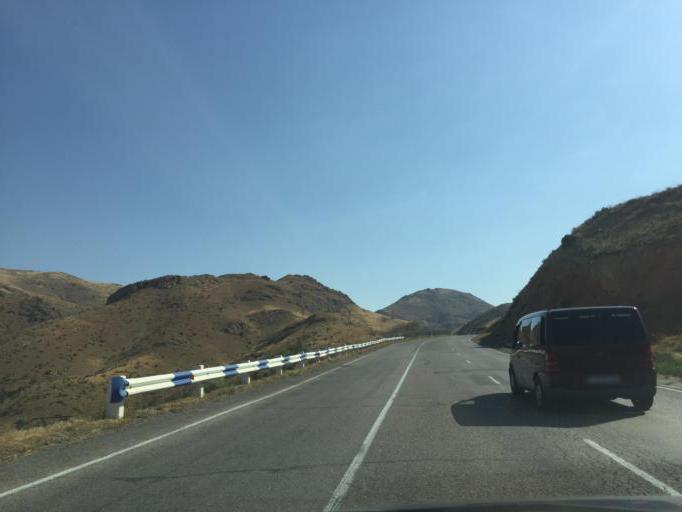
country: AM
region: Ararat
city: Zangakatun
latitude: 39.7951
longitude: 44.9563
